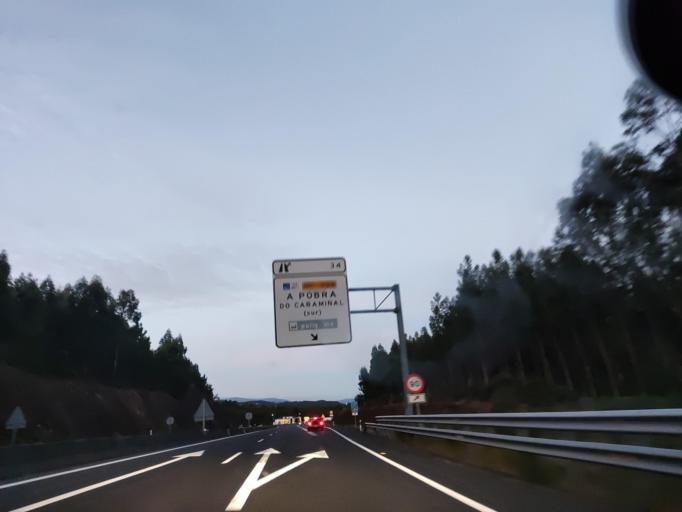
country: ES
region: Galicia
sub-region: Provincia da Coruna
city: Boiro
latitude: 42.6054
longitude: -8.9683
